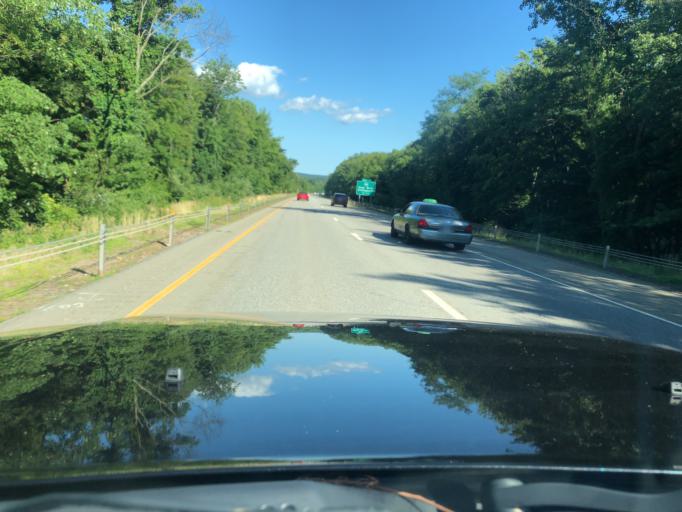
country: US
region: Connecticut
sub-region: Middlesex County
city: Chester Center
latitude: 41.3900
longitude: -72.4586
